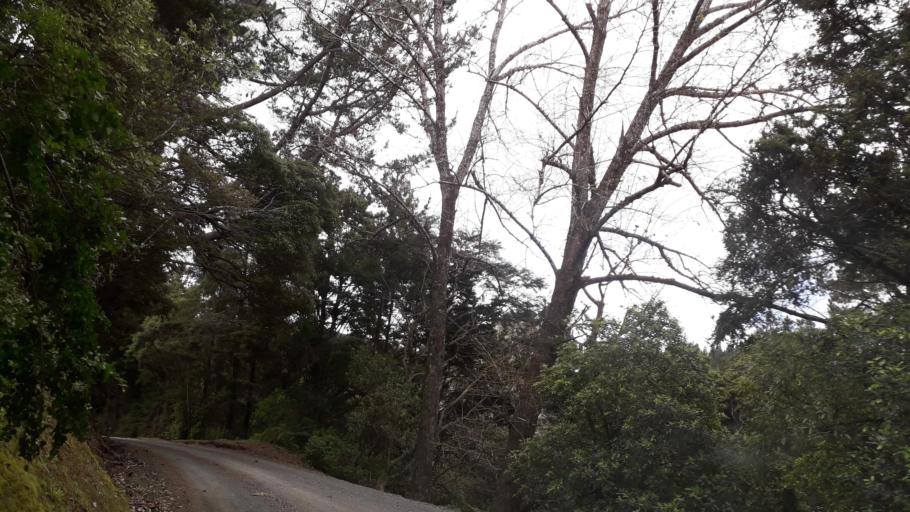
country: NZ
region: Northland
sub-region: Far North District
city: Taipa
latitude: -35.0729
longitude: 173.5549
